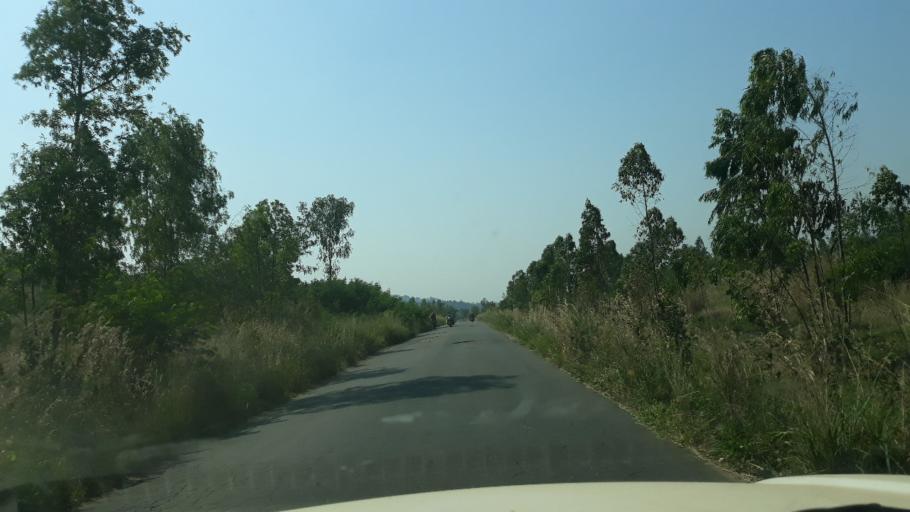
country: CD
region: South Kivu
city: Uvira
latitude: -3.2555
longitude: 29.1612
